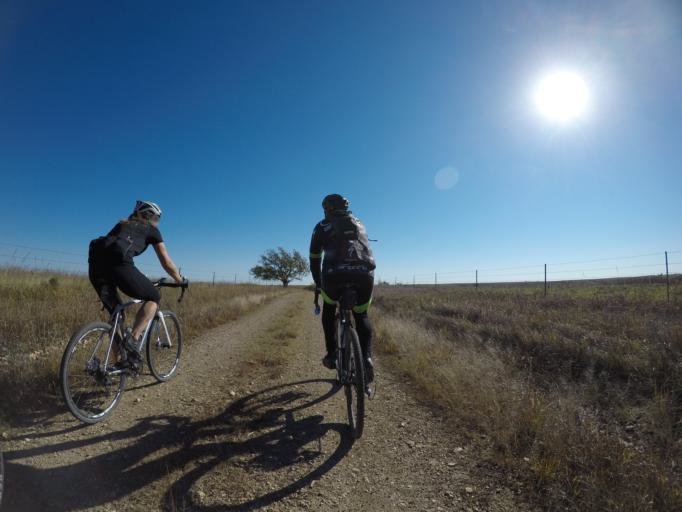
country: US
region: Kansas
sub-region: Wabaunsee County
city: Alma
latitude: 38.8853
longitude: -96.3856
